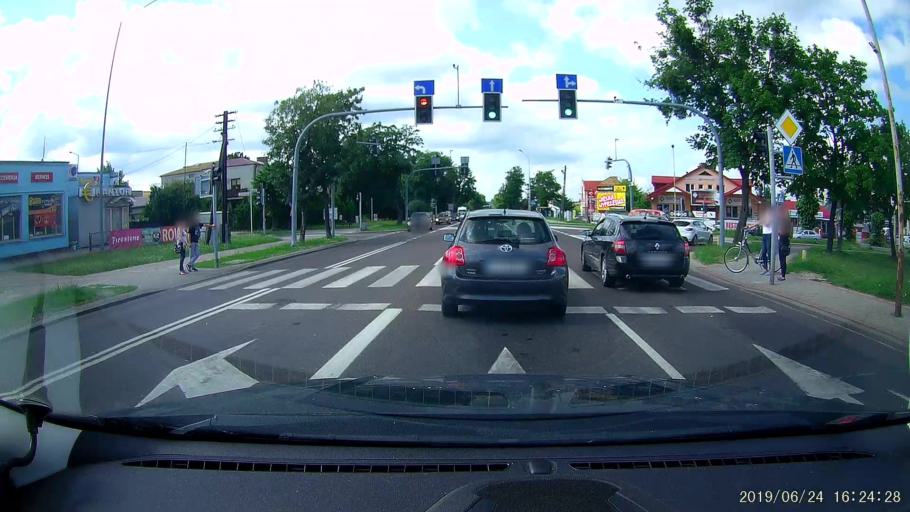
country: PL
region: Lublin Voivodeship
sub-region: Powiat tomaszowski
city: Tomaszow Lubelski
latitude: 50.4360
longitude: 23.4201
